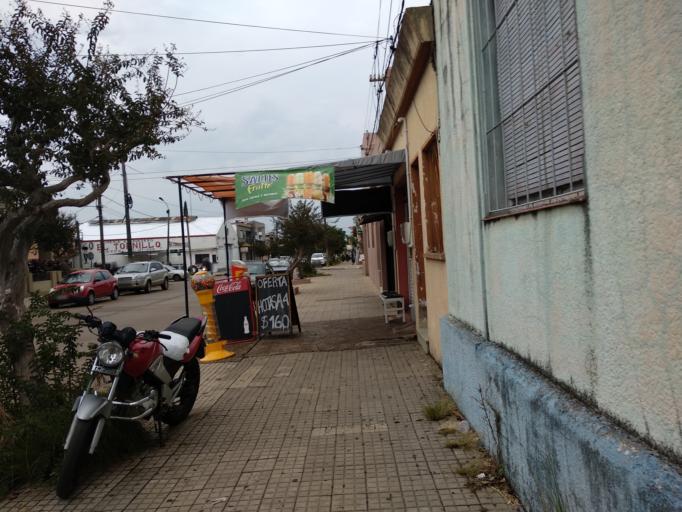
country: UY
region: Artigas
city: Artigas
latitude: -30.4035
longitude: -56.4661
